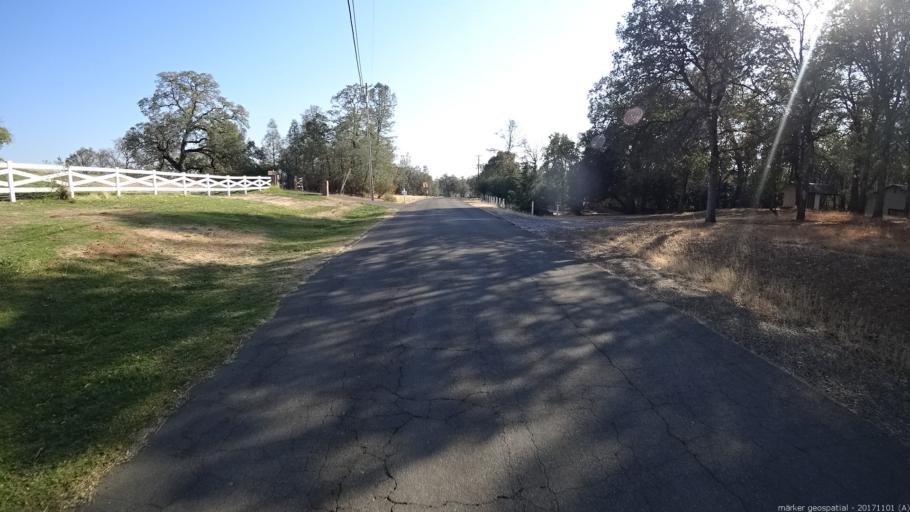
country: US
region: California
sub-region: Shasta County
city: Shasta Lake
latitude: 40.6724
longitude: -122.3008
